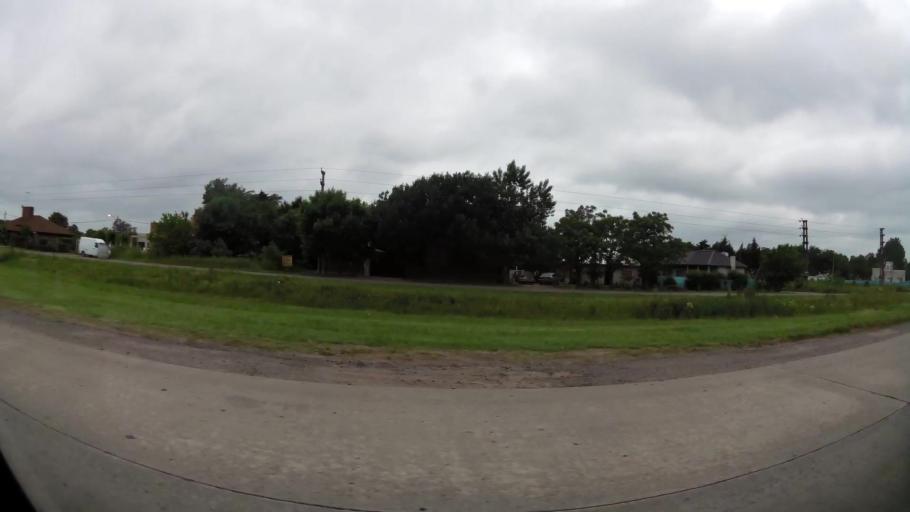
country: AR
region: Buenos Aires
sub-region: Partido de La Plata
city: La Plata
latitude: -35.0335
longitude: -58.0901
